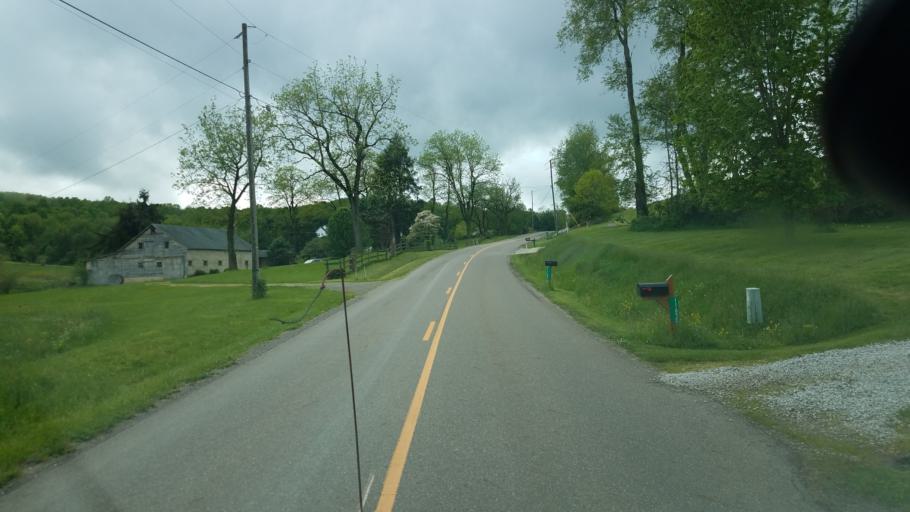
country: US
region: Ohio
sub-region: Tuscarawas County
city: Strasburg
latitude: 40.6411
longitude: -81.4686
